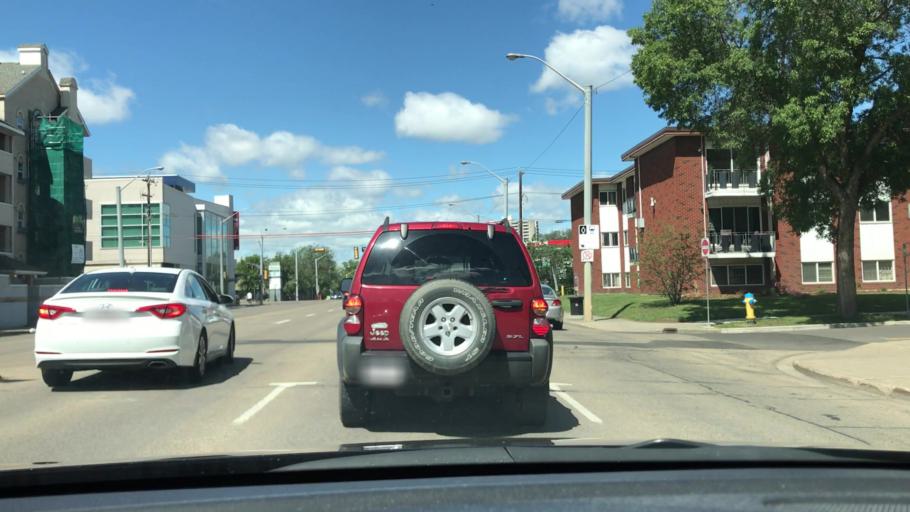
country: CA
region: Alberta
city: Edmonton
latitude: 53.5169
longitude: -113.5120
